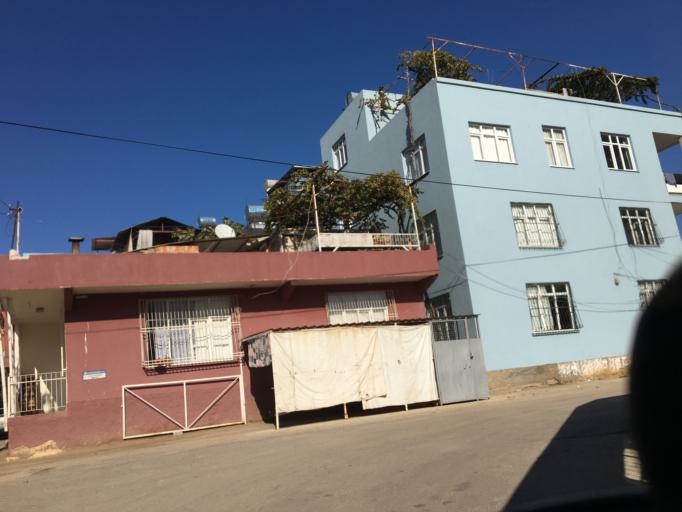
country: TR
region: Adana
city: Seyhan
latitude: 37.0122
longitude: 35.2919
